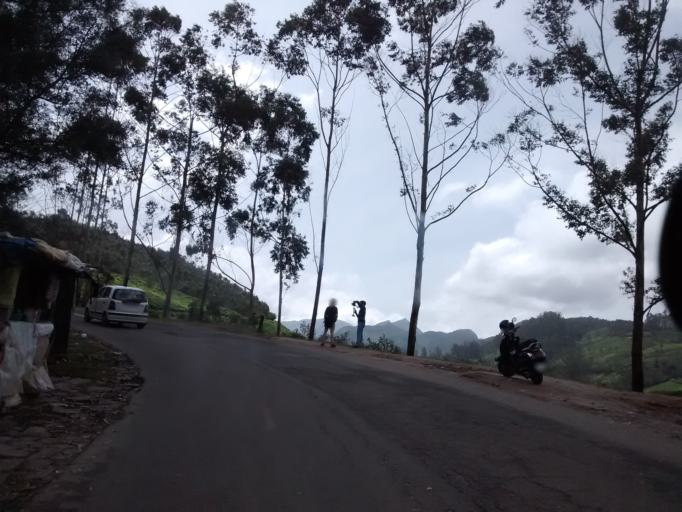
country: IN
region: Kerala
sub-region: Idukki
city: Munnar
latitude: 10.0857
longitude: 77.0779
